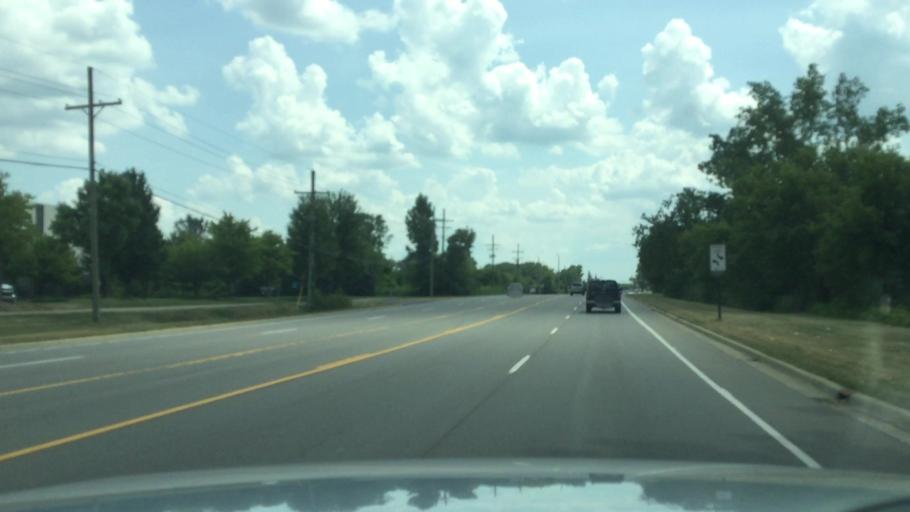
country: US
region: Michigan
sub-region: Washtenaw County
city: Ypsilanti
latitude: 42.2223
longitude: -83.6182
